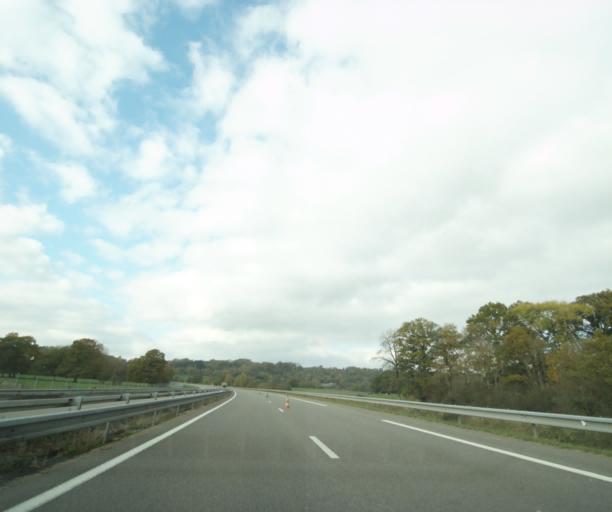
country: FR
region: Lorraine
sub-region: Departement de la Meuse
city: Clermont-en-Argonne
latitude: 49.0959
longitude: 5.0832
